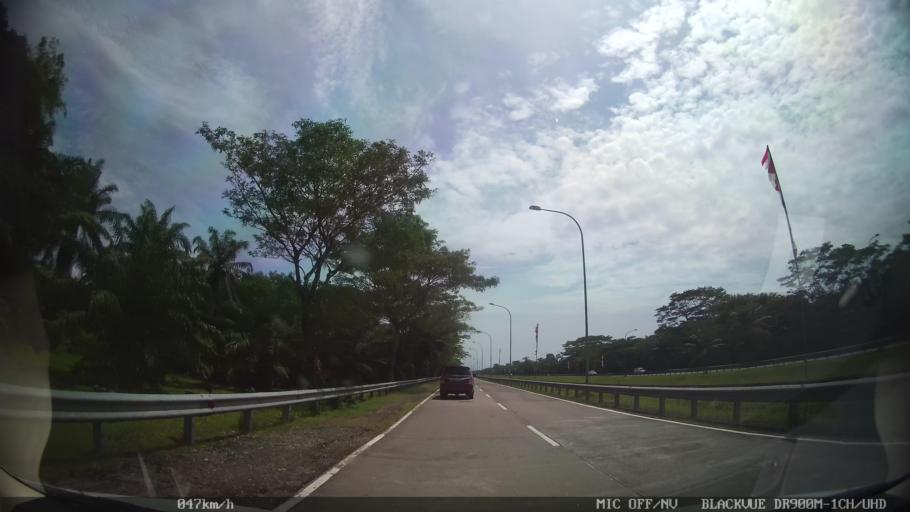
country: ID
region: North Sumatra
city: Percut
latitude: 3.6177
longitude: 98.8611
